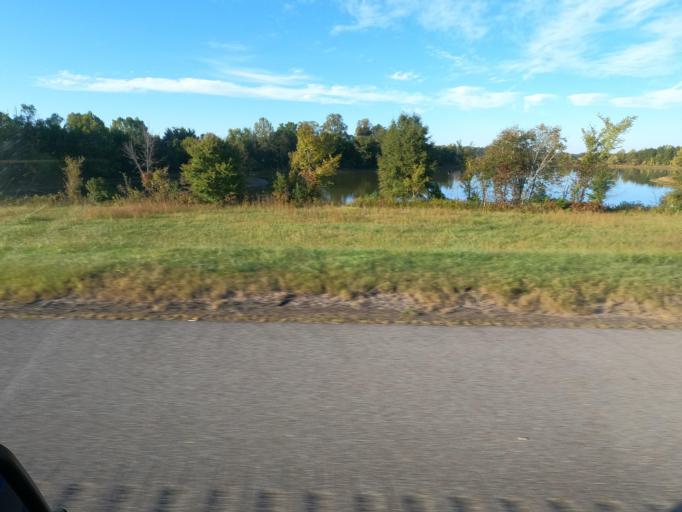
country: US
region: Tennessee
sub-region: Shelby County
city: Millington
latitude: 35.3087
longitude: -89.8132
